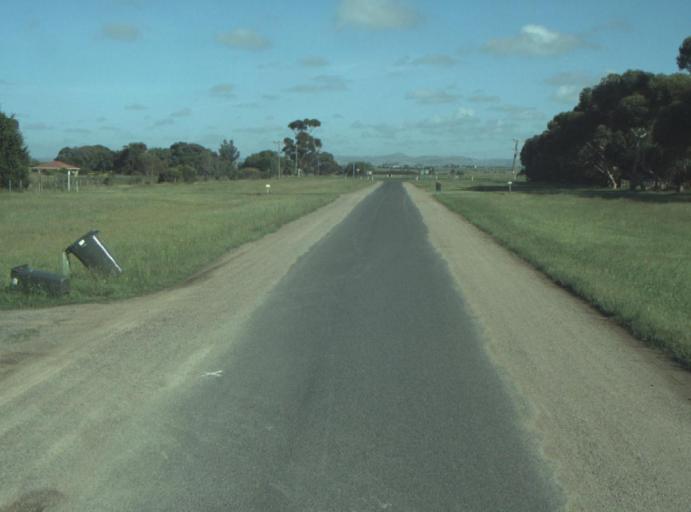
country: AU
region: Victoria
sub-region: Greater Geelong
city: Lara
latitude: -38.0086
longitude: 144.3827
